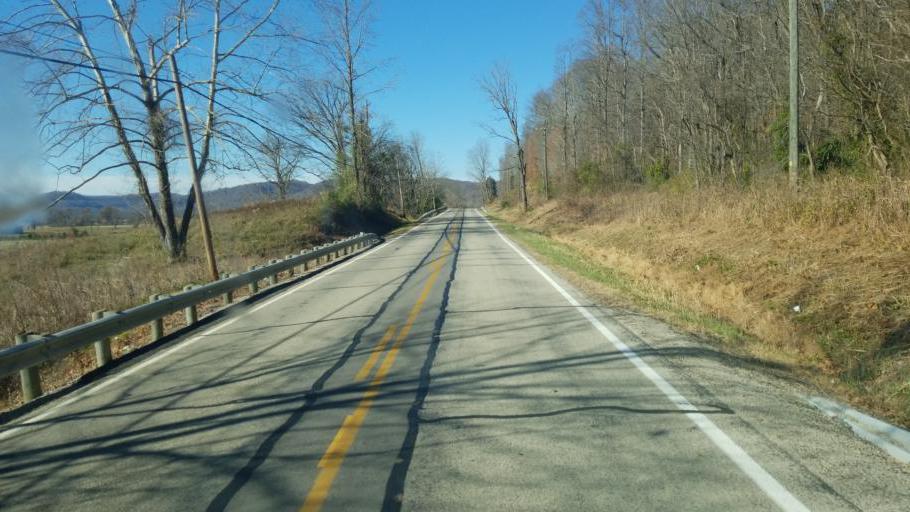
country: US
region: Kentucky
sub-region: Lewis County
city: Vanceburg
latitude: 38.6283
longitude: -83.2037
